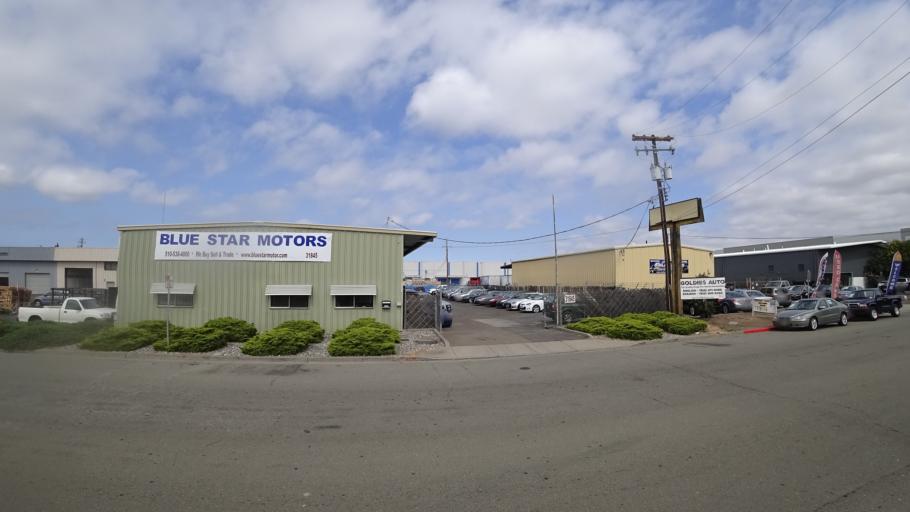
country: US
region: California
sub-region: Alameda County
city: Union City
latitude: 37.6077
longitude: -122.0453
